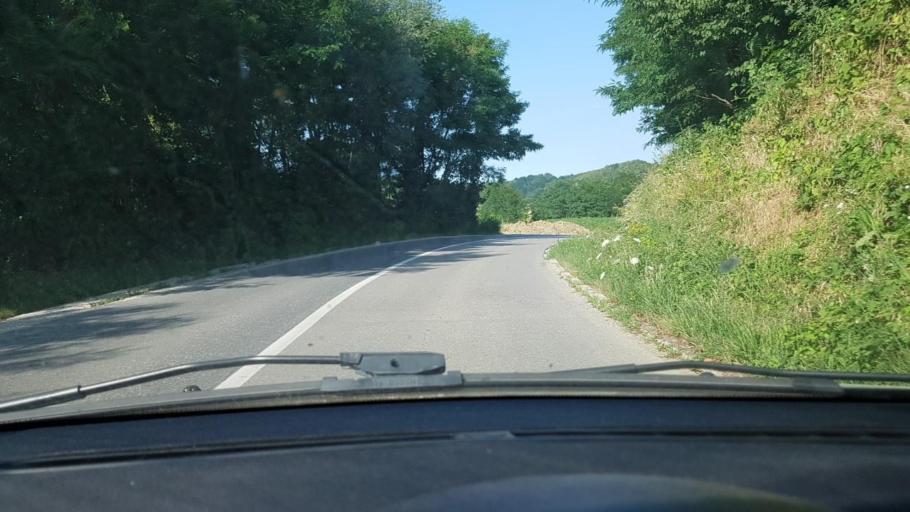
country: HR
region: Krapinsko-Zagorska
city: Radoboj
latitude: 46.2086
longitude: 15.9197
